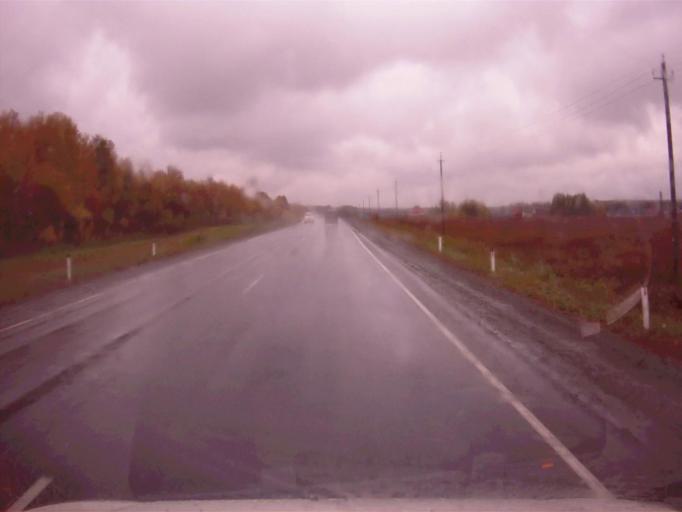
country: RU
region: Chelyabinsk
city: Argayash
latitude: 55.4048
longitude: 61.0624
